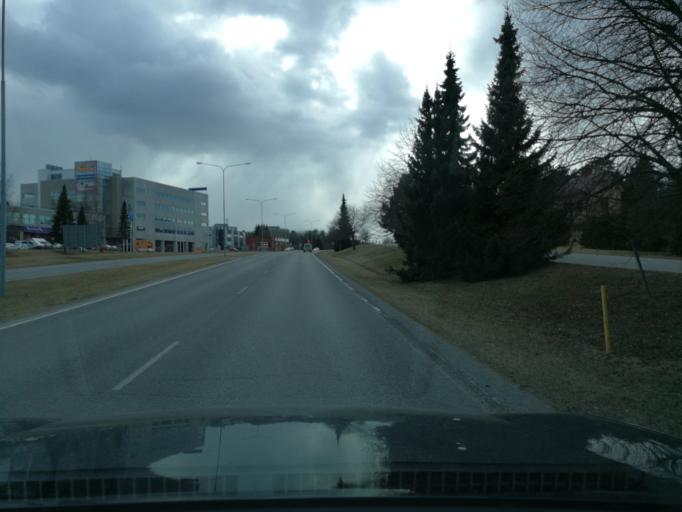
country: FI
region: Varsinais-Suomi
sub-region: Turku
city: Turku
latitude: 60.4634
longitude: 22.3315
